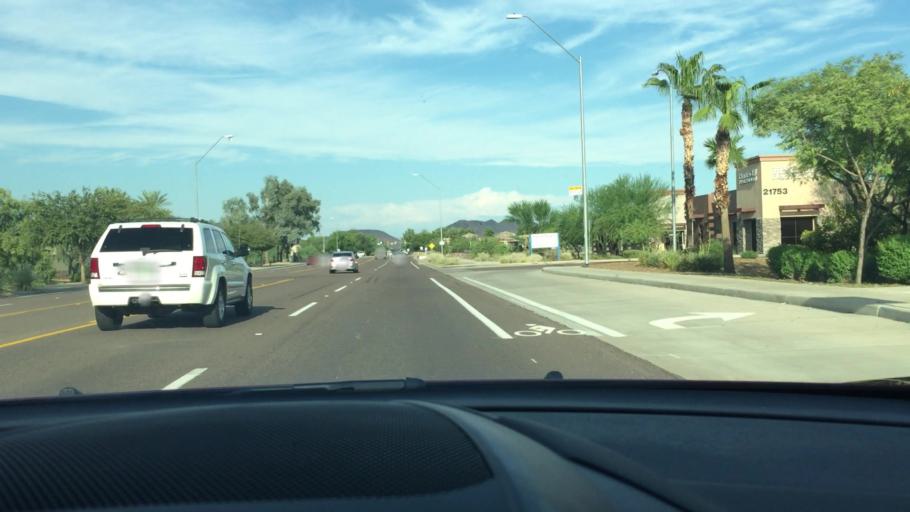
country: US
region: Arizona
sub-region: Maricopa County
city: Sun City
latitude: 33.6816
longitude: -112.2251
